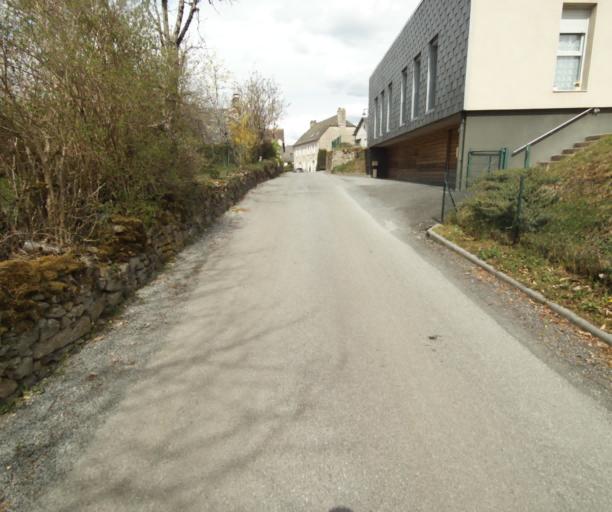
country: FR
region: Limousin
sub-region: Departement de la Correze
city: Laguenne
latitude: 45.2184
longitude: 1.8950
